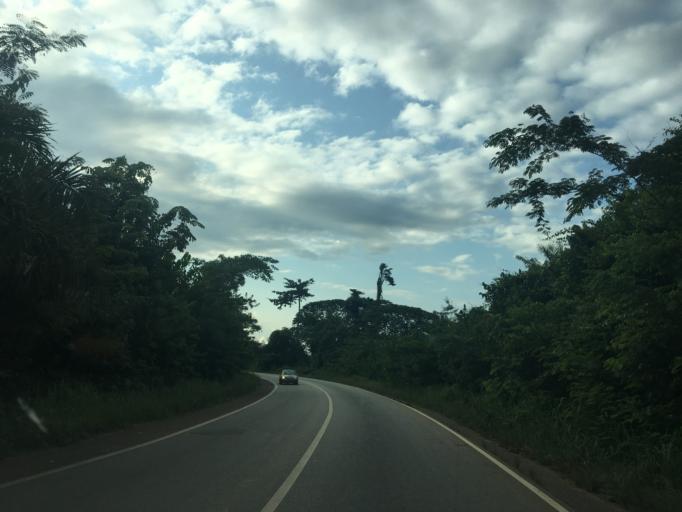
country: GH
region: Western
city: Bibiani
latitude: 6.4182
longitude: -2.3020
